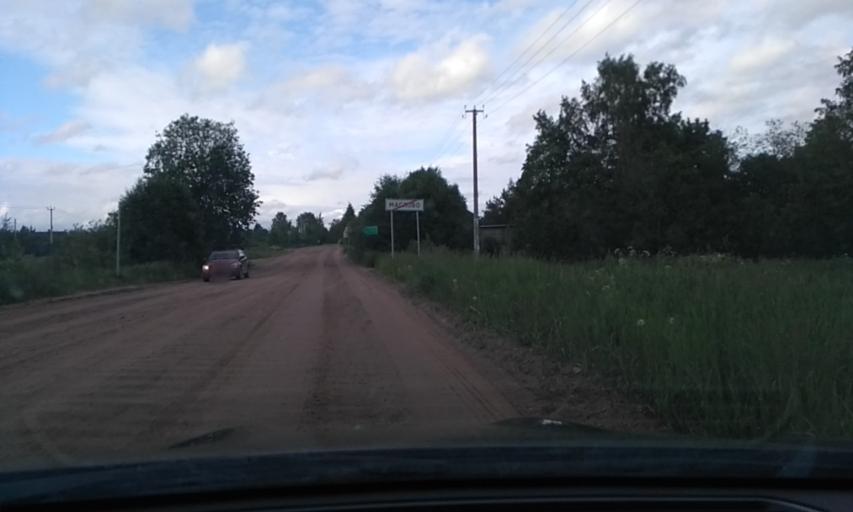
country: RU
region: Leningrad
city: Otradnoye
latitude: 59.7929
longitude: 30.7954
